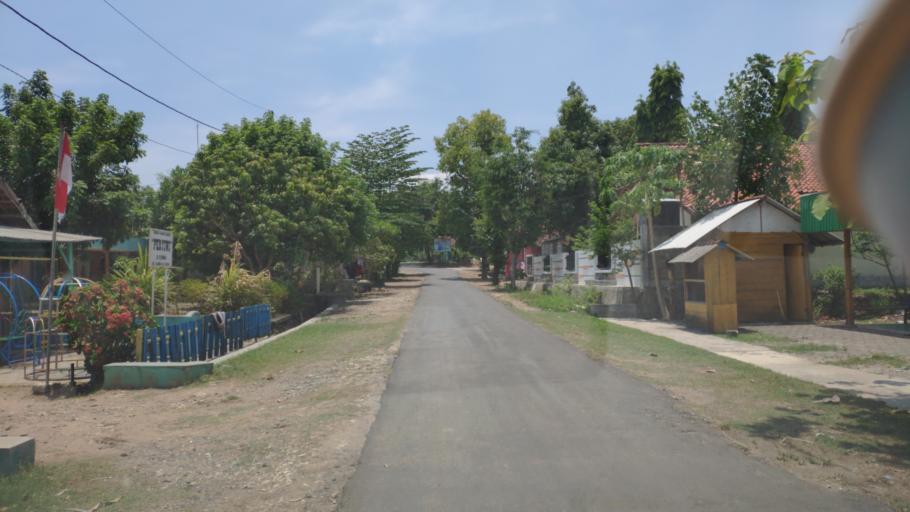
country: ID
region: Central Java
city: Plumbon
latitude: -7.0515
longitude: 111.2911
